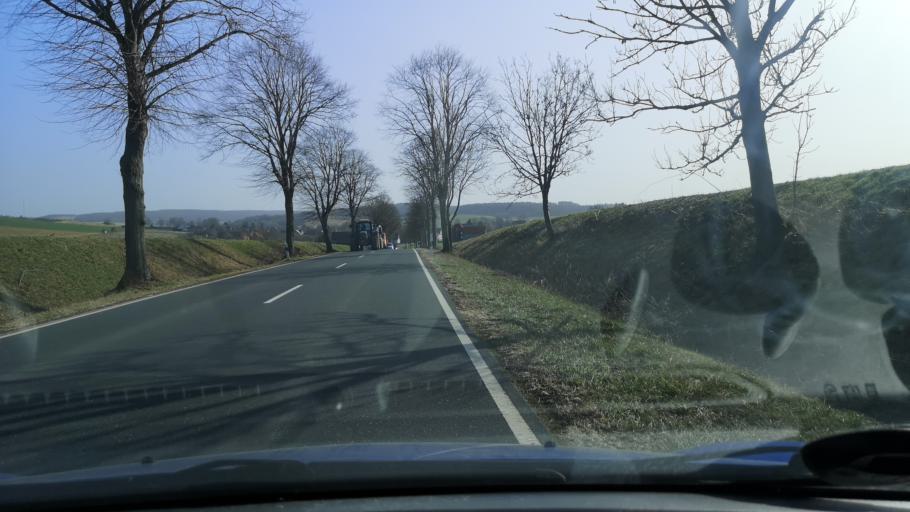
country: DE
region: Lower Saxony
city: Weenzen
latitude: 52.0286
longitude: 9.6196
